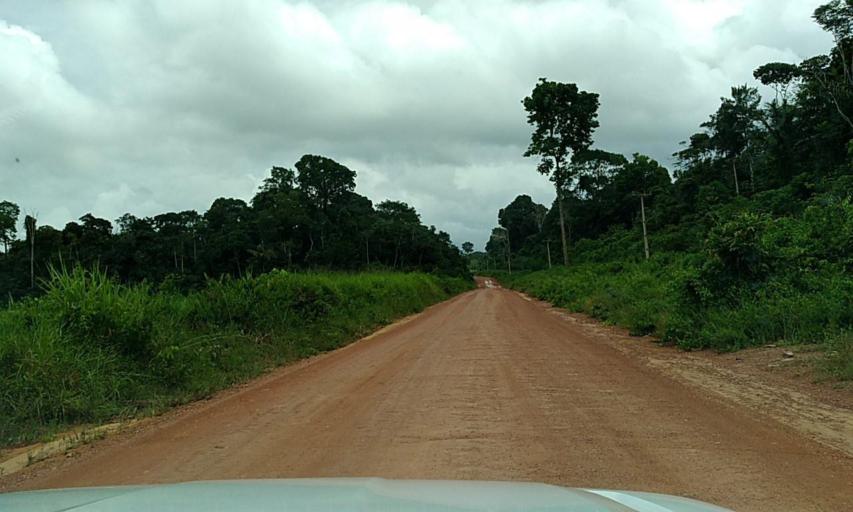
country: BR
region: Para
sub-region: Senador Jose Porfirio
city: Senador Jose Porfirio
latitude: -2.6786
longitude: -51.8327
